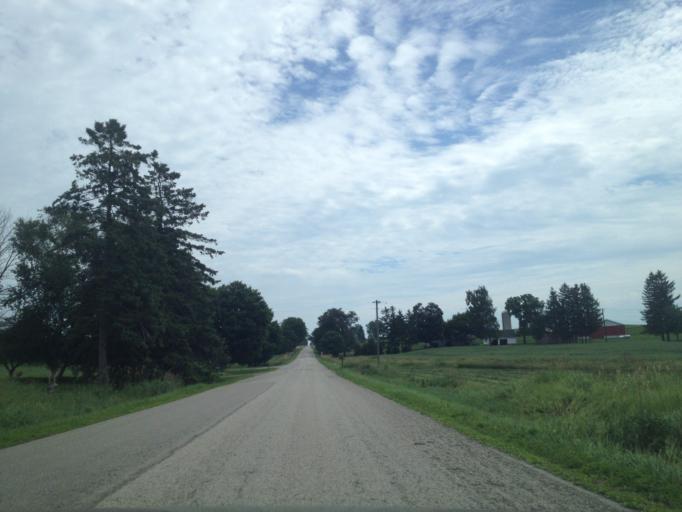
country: CA
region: Ontario
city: Ingersoll
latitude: 42.9765
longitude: -80.7710
